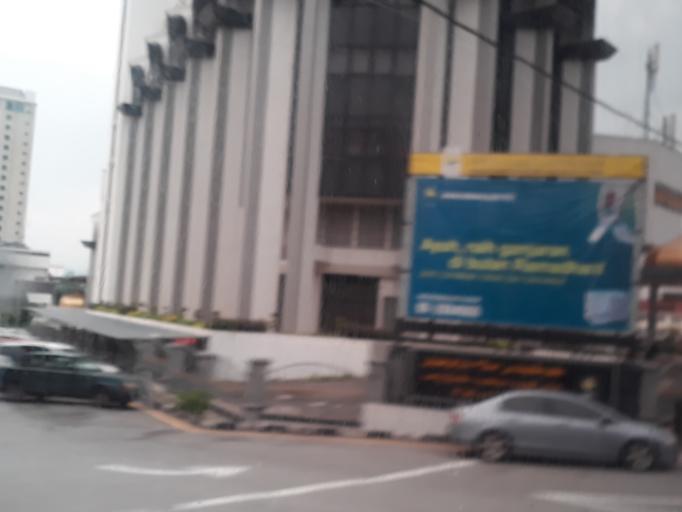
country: MY
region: Perak
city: Ipoh
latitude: 4.6034
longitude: 101.0771
